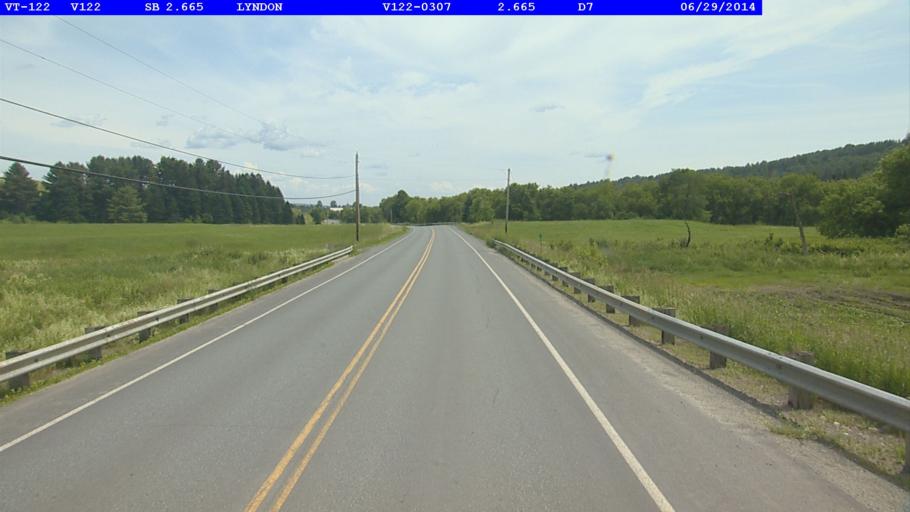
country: US
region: Vermont
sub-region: Caledonia County
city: Lyndonville
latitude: 44.5632
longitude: -72.0396
